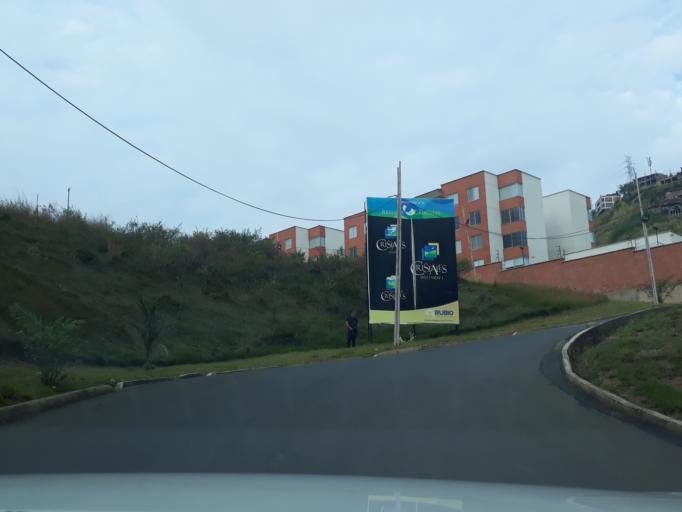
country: CO
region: Valle del Cauca
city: Cali
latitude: 3.4331
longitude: -76.5528
